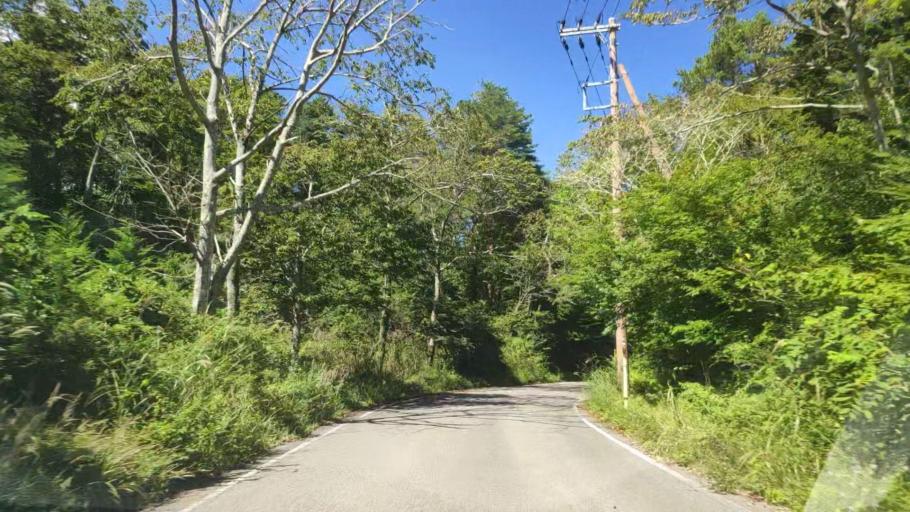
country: JP
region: Shizuoka
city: Gotemba
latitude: 35.3970
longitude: 138.8622
